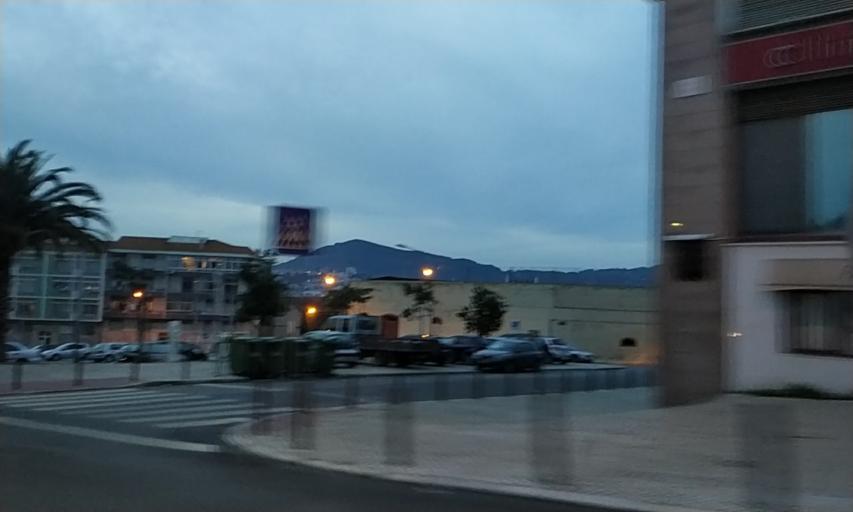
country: PT
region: Setubal
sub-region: Setubal
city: Setubal
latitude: 38.5295
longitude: -8.8817
